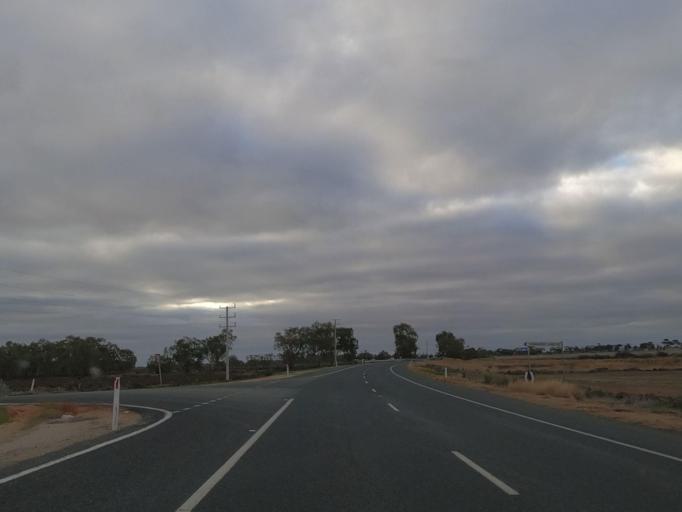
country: AU
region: Victoria
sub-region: Swan Hill
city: Swan Hill
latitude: -35.6212
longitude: 143.8037
